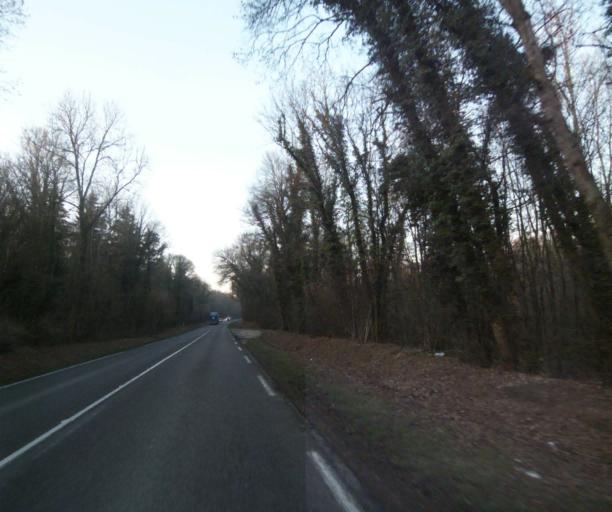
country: FR
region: Lorraine
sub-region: Departement de la Meuse
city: Ancerville
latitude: 48.6156
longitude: 4.9978
